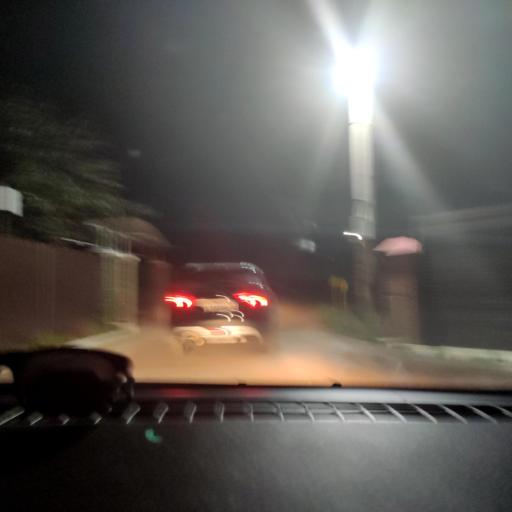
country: RU
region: Samara
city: Volzhskiy
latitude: 53.4436
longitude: 50.0784
